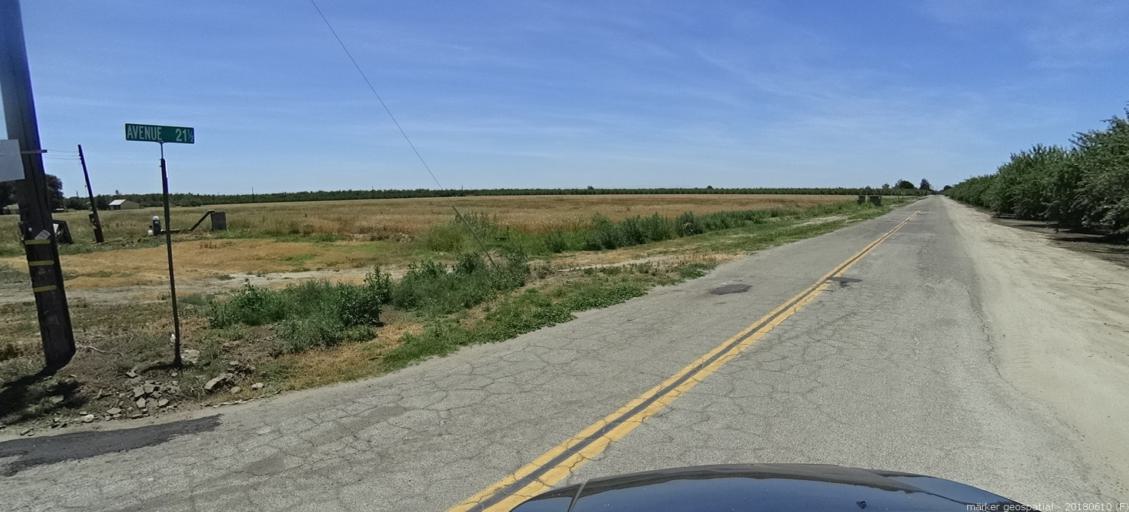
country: US
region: California
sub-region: Madera County
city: Chowchilla
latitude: 37.0618
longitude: -120.2927
